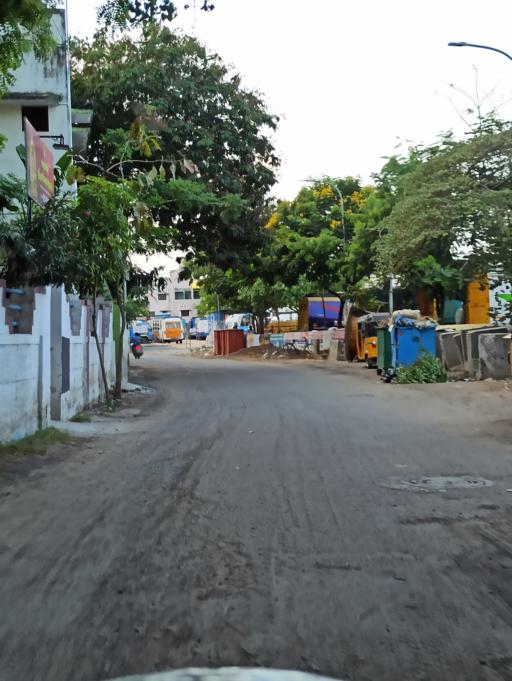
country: IN
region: Tamil Nadu
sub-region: Chennai
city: Chetput
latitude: 13.0552
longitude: 80.2078
